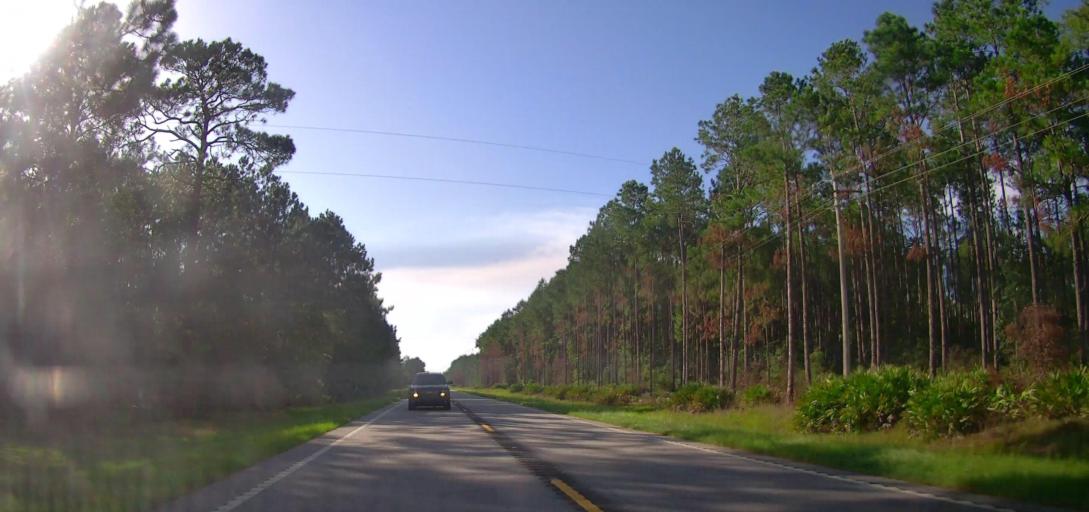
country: US
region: Georgia
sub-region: Coffee County
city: Nicholls
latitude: 31.4427
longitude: -82.7182
